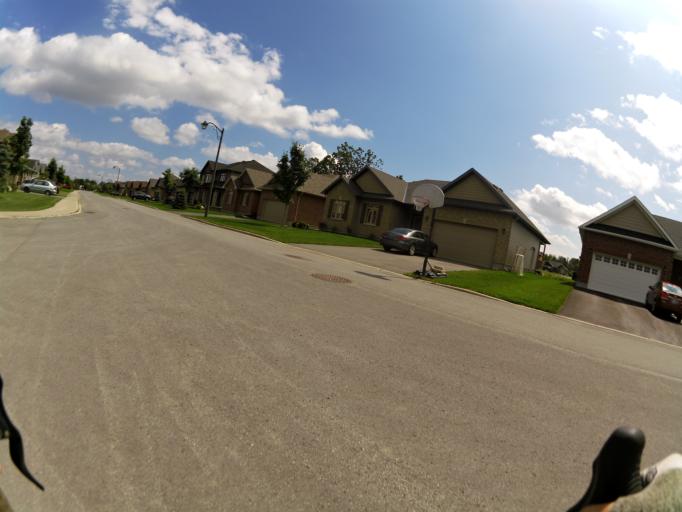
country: CA
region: Ontario
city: Bells Corners
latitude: 45.1953
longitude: -75.8493
